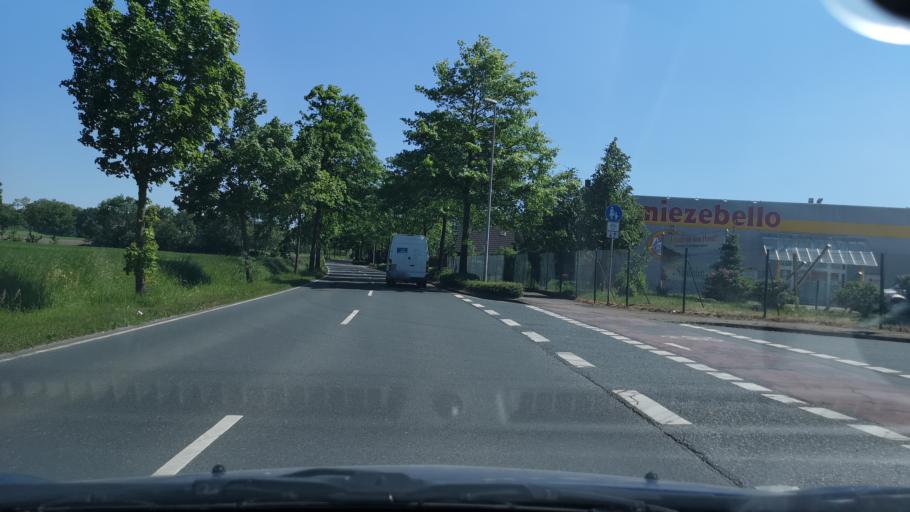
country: DE
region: Lower Saxony
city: Garbsen-Mitte
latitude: 52.4442
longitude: 9.6162
